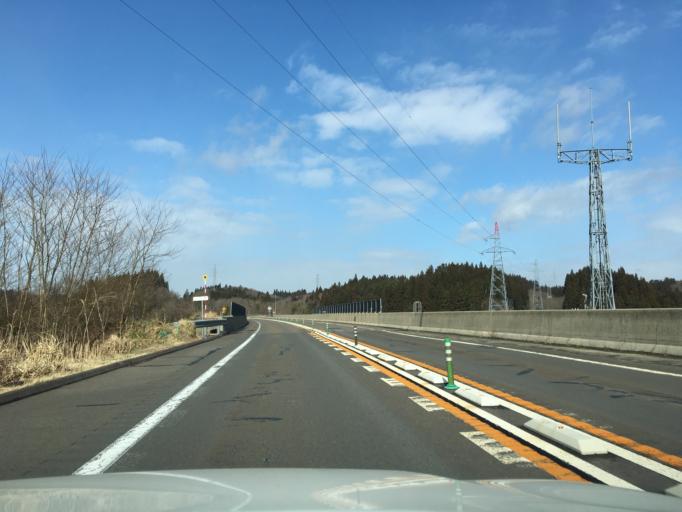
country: JP
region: Akita
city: Akita
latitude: 39.7390
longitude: 140.1713
